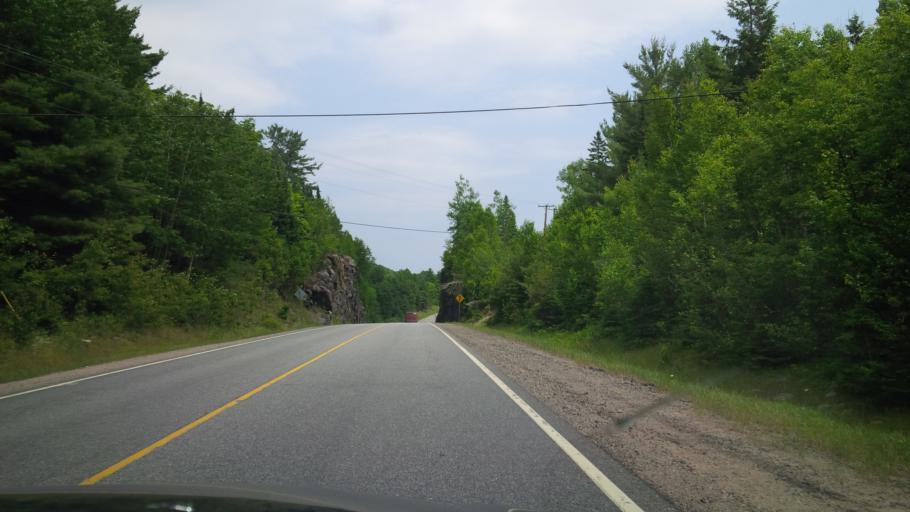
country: CA
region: Ontario
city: Huntsville
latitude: 45.5433
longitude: -79.2619
